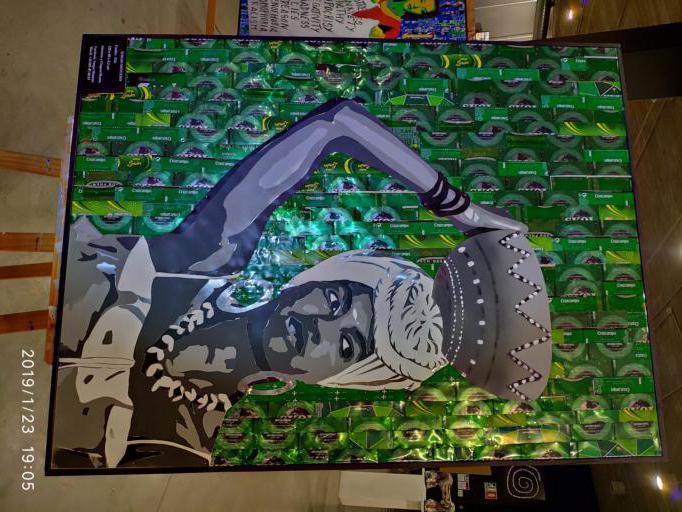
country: ES
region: Andalusia
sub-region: Provincia de Malaga
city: Malaga
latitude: 36.7188
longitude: -4.4134
